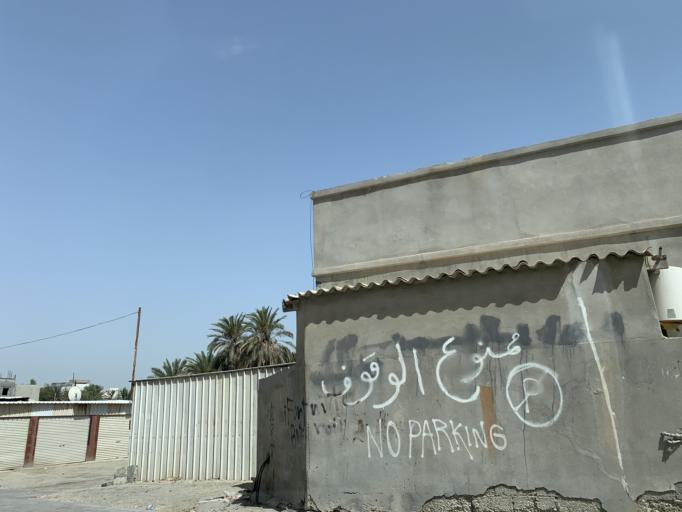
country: BH
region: Northern
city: Sitrah
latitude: 26.1462
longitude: 50.6080
